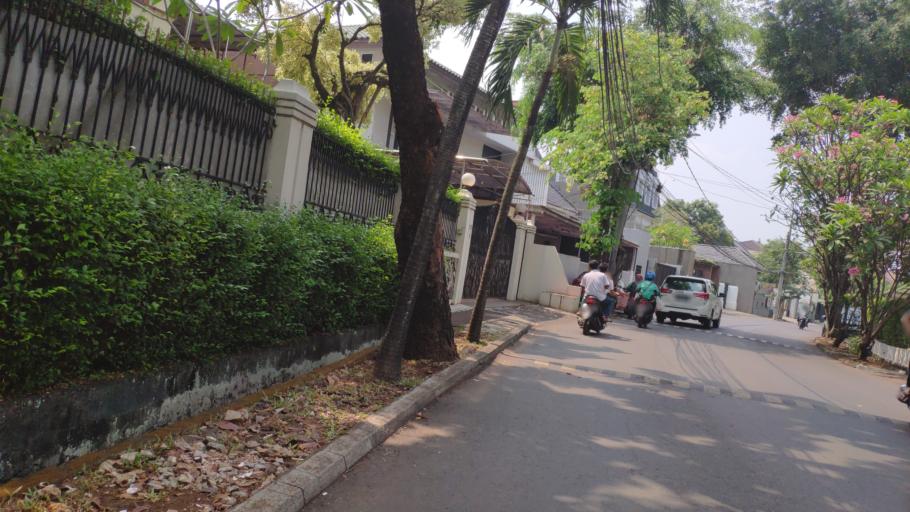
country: ID
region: West Java
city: Pamulang
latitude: -6.2969
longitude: 106.7996
